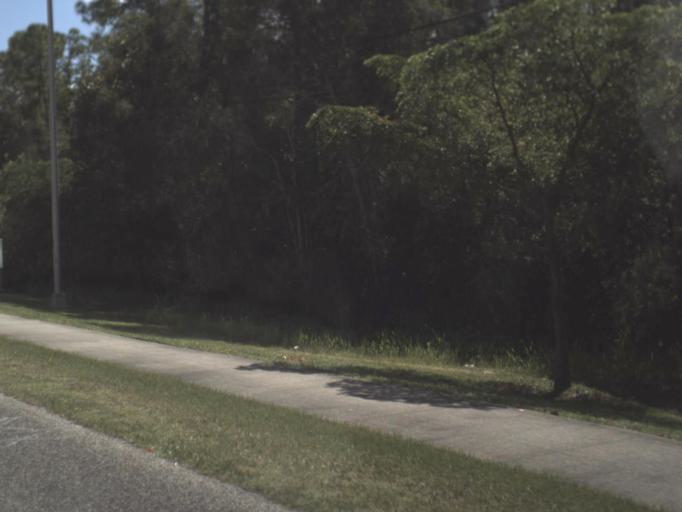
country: US
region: Florida
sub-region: Collier County
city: Lely Resort
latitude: 26.0716
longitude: -81.7125
